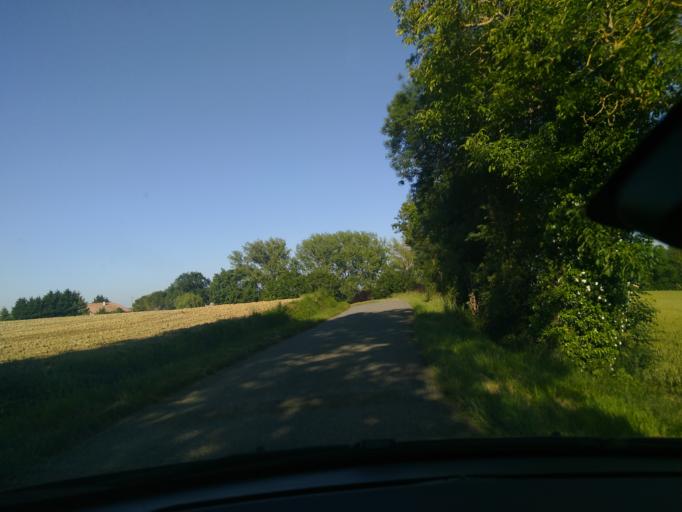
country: FR
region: Midi-Pyrenees
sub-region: Departement du Tarn-et-Garonne
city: Beaumont-de-Lomagne
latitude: 43.7787
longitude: 0.9560
